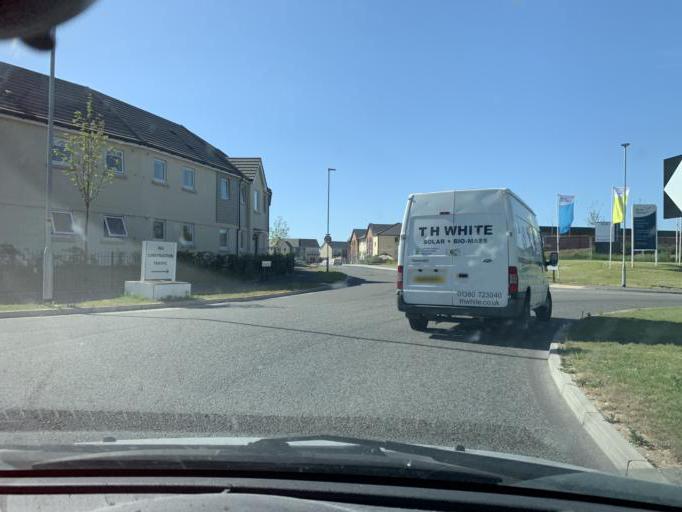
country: GB
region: England
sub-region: Wiltshire
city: Durnford
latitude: 51.1072
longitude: -1.7934
